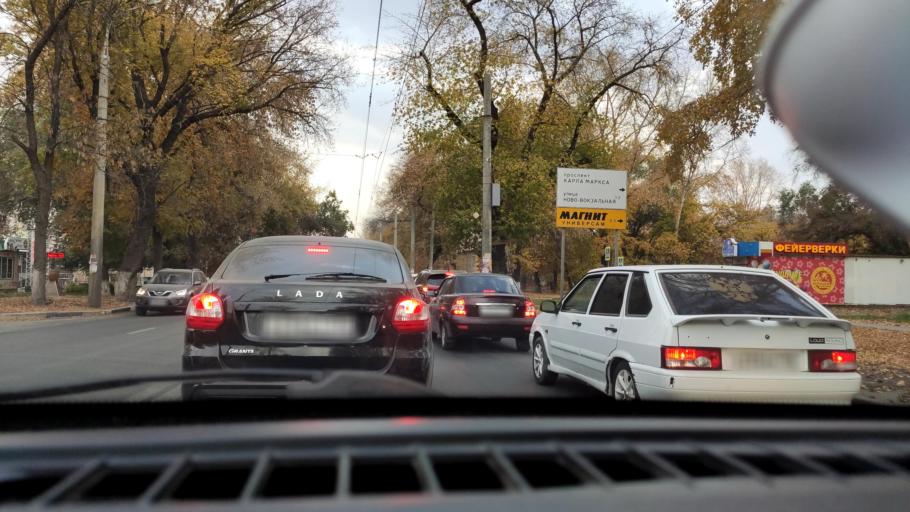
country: RU
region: Samara
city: Samara
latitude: 53.2381
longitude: 50.2389
